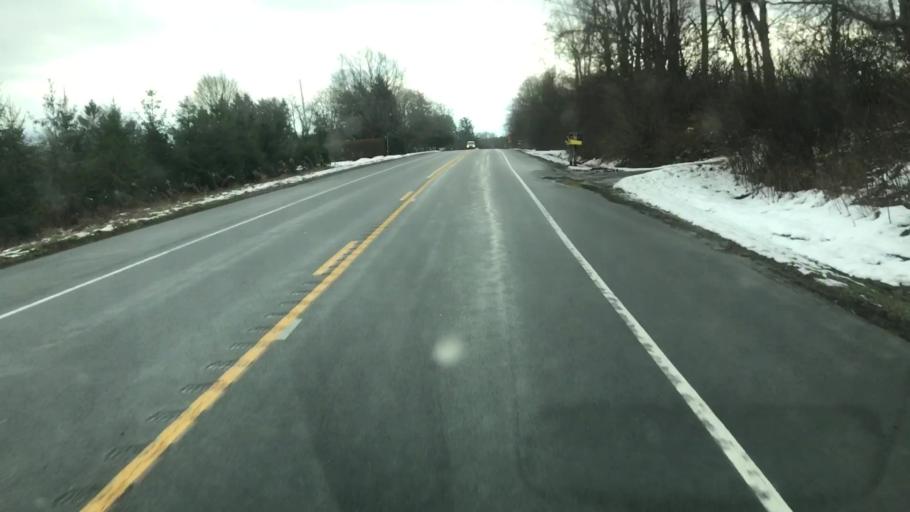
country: US
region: New York
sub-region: Onondaga County
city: Skaneateles
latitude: 42.9061
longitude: -76.4246
